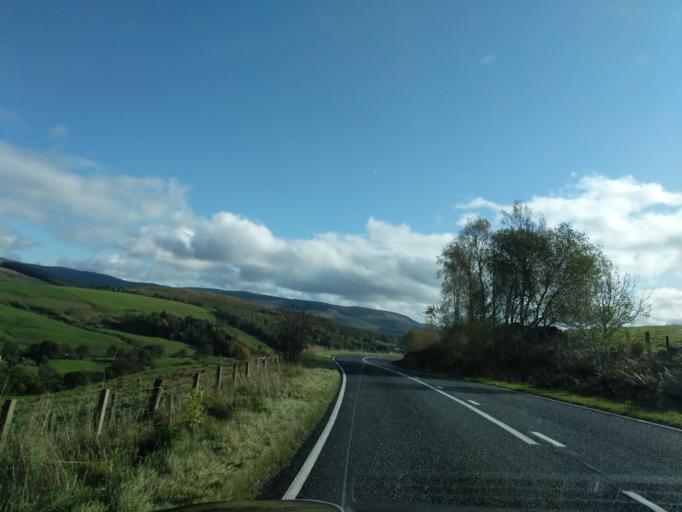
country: GB
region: Scotland
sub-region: Dumfries and Galloway
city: Moffat
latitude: 55.3528
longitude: -3.4667
